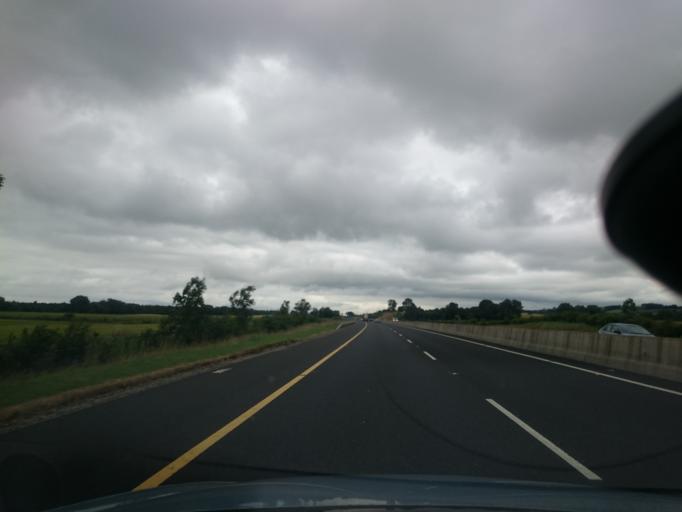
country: IE
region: Leinster
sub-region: Kildare
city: Moone
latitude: 53.0419
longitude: -6.7938
